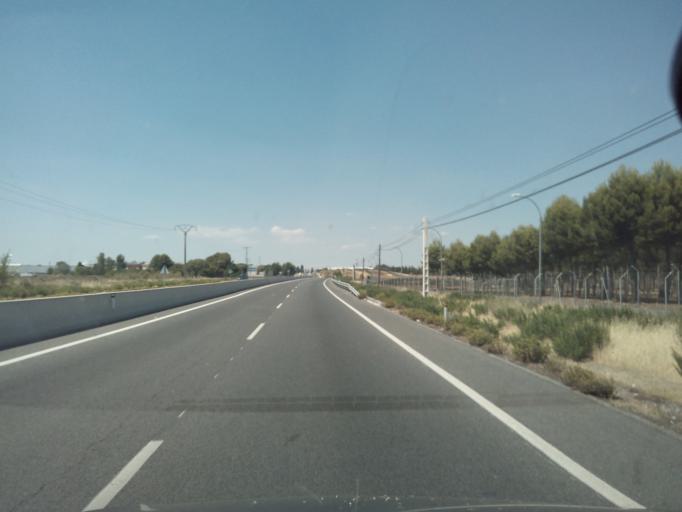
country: ES
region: Madrid
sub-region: Provincia de Madrid
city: Ajalvir
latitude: 40.4937
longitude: -3.4788
